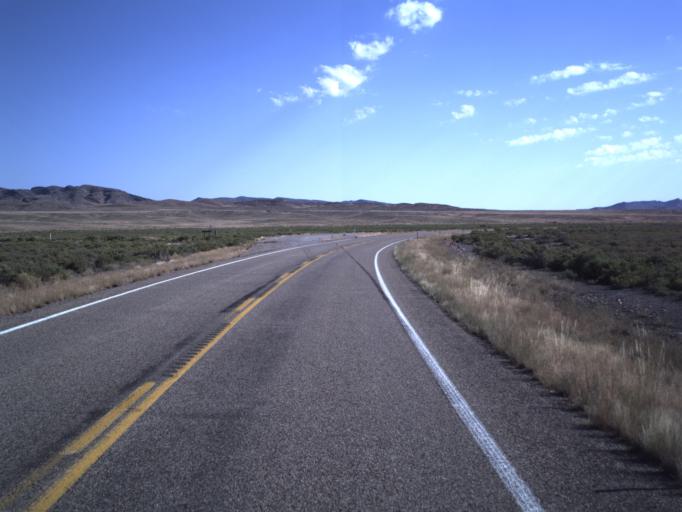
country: US
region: Utah
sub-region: Beaver County
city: Milford
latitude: 38.7323
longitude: -112.9659
